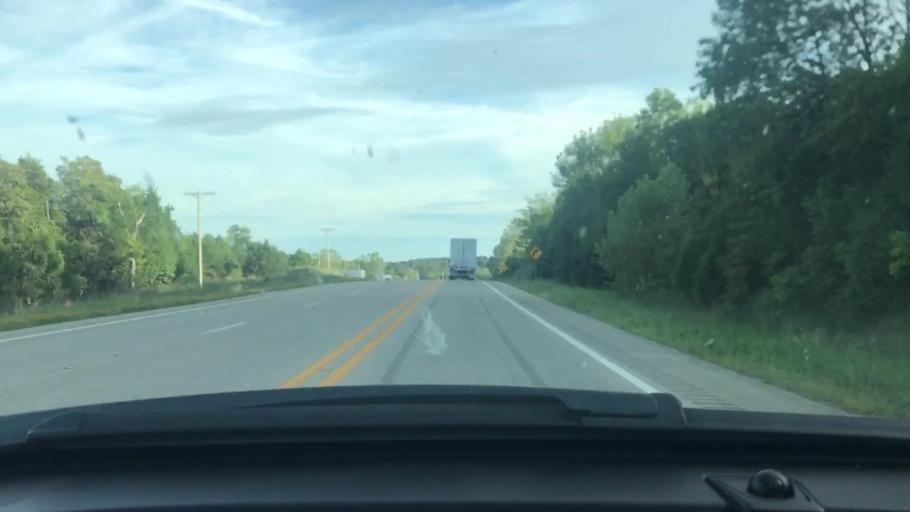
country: US
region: Arkansas
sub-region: Lawrence County
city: Hoxie
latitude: 36.1458
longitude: -91.1591
